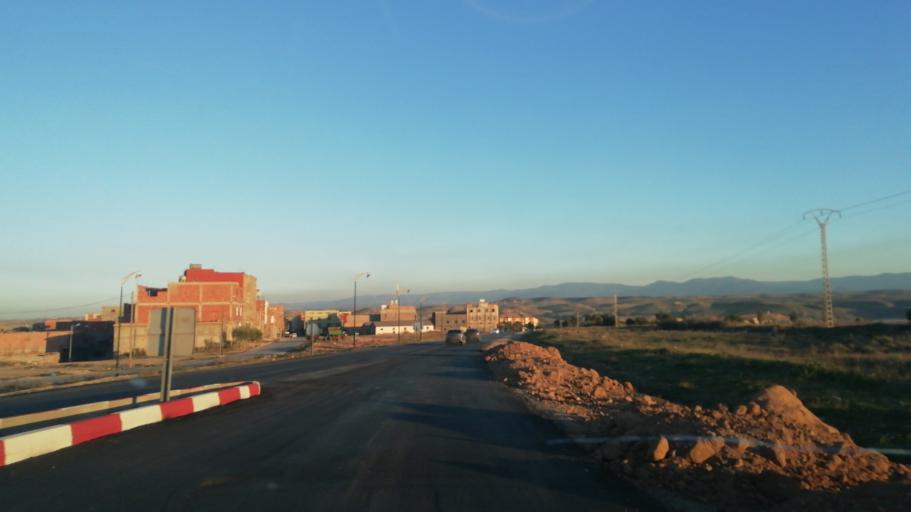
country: DZ
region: Tlemcen
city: Nedroma
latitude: 34.8924
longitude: -1.6598
